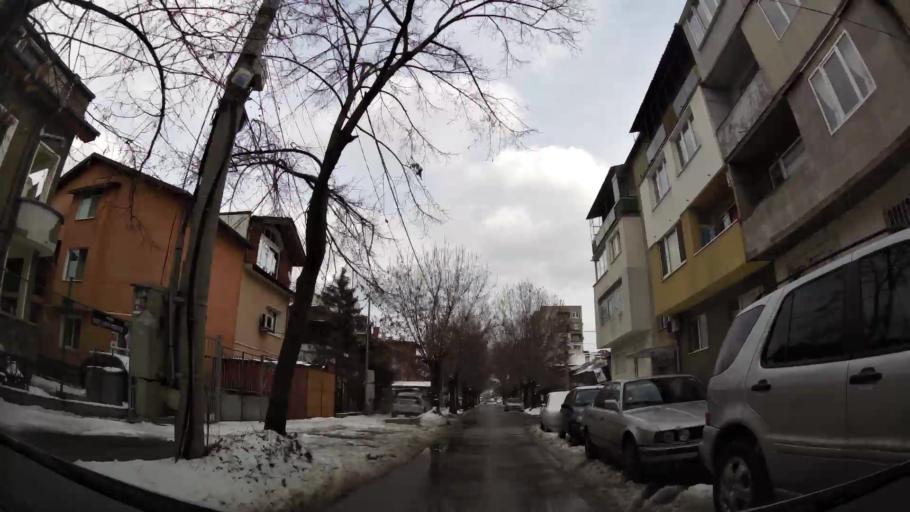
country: BG
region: Sofia-Capital
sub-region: Stolichna Obshtina
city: Sofia
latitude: 42.7027
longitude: 23.3700
